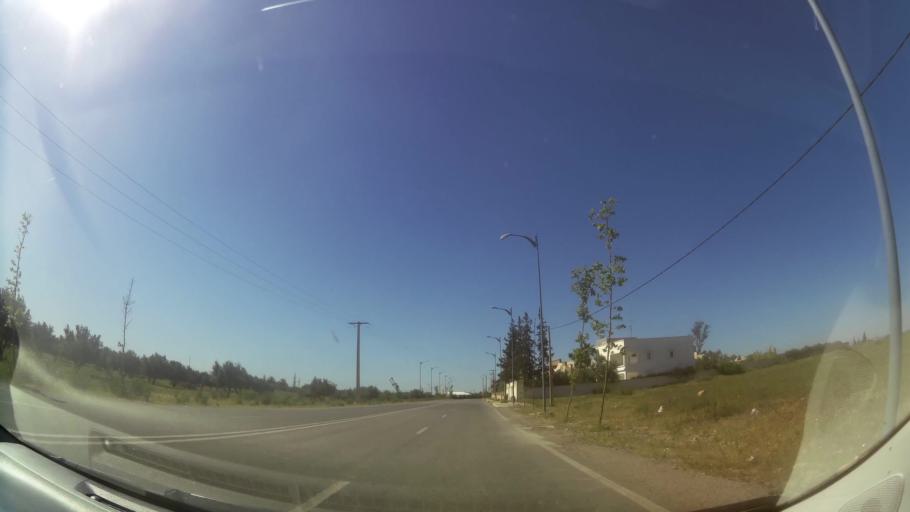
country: MA
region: Oriental
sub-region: Oujda-Angad
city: Oujda
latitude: 34.7266
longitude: -1.8687
